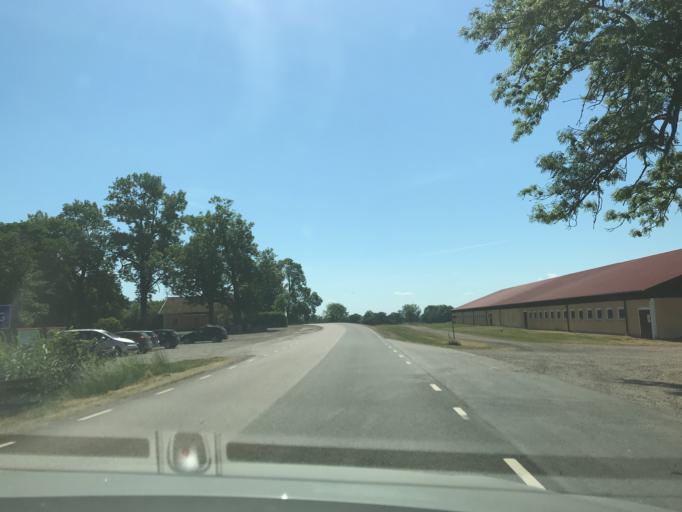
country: SE
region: Vaestra Goetaland
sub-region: Gotene Kommun
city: Kallby
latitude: 58.5478
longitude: 13.3331
